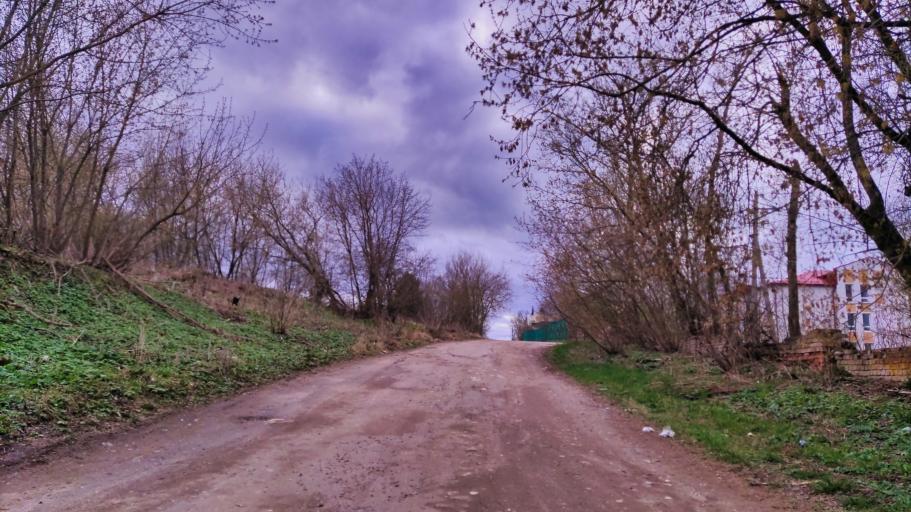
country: RU
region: Tverskaya
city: Rzhev
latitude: 56.2565
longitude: 34.3346
